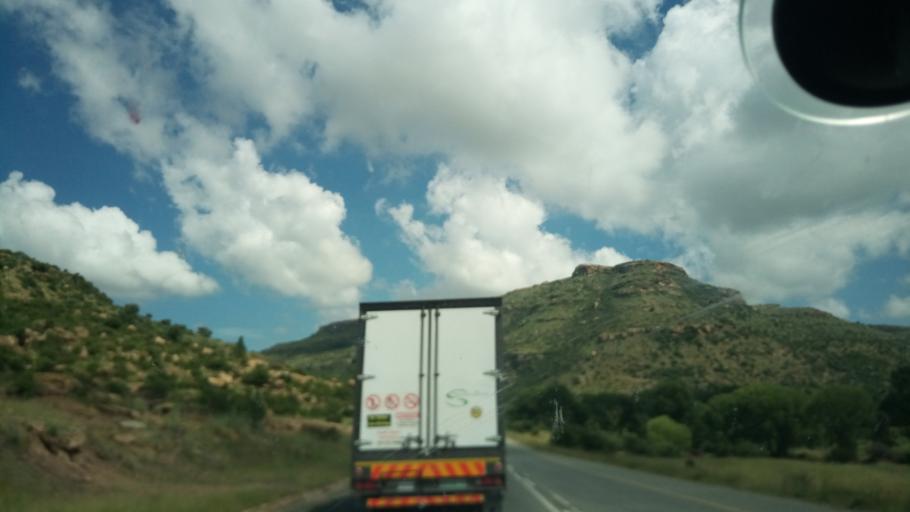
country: ZA
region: Orange Free State
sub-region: Thabo Mofutsanyana District Municipality
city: Ficksburg
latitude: -28.8887
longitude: 27.8384
